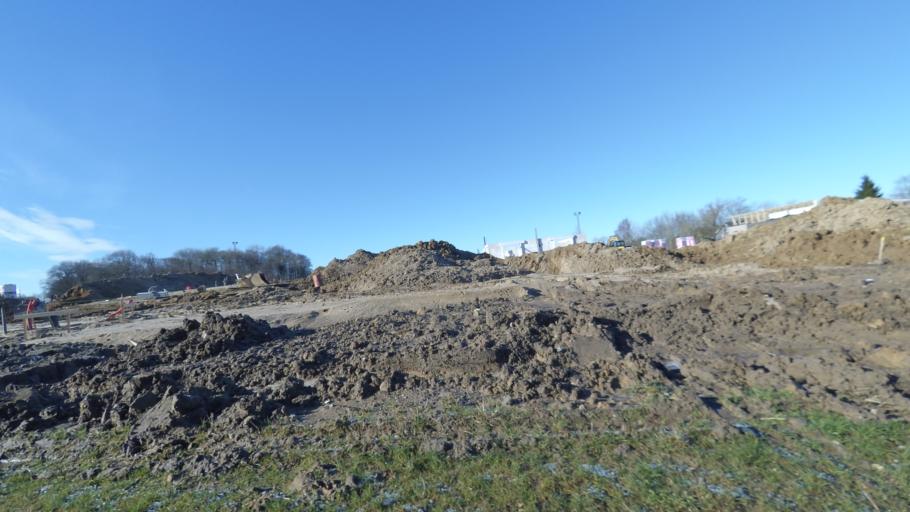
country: DK
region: Central Jutland
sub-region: Arhus Kommune
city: Kolt
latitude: 56.1138
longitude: 10.0862
